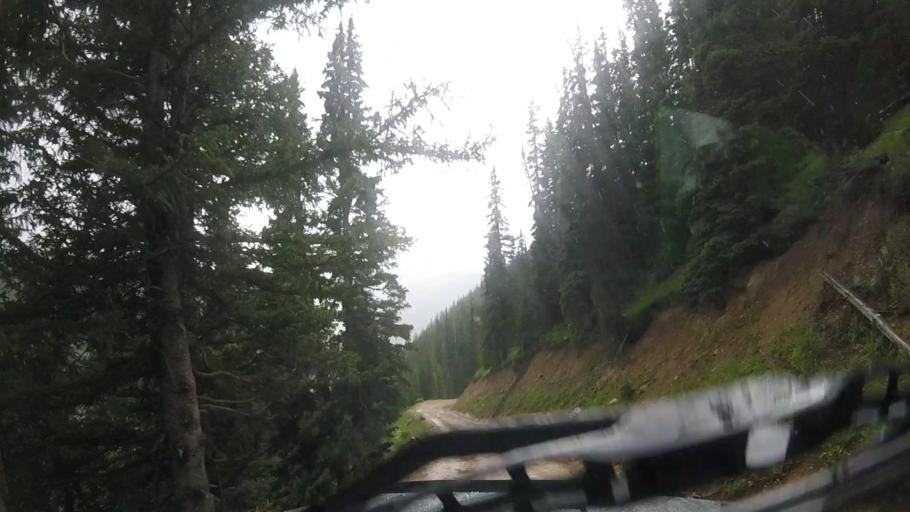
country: US
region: Colorado
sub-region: San Juan County
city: Silverton
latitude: 37.9036
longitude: -107.6471
